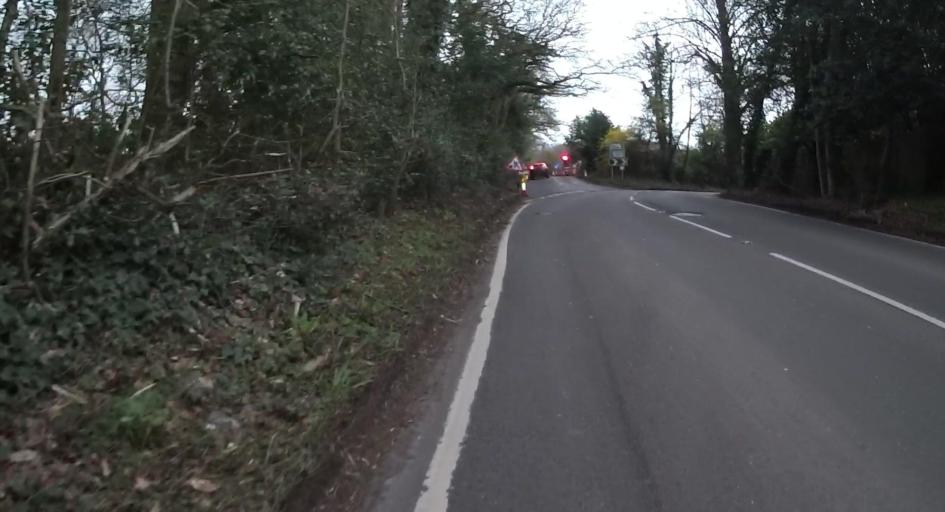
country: GB
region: England
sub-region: Surrey
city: Farnham
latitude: 51.1758
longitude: -0.7902
